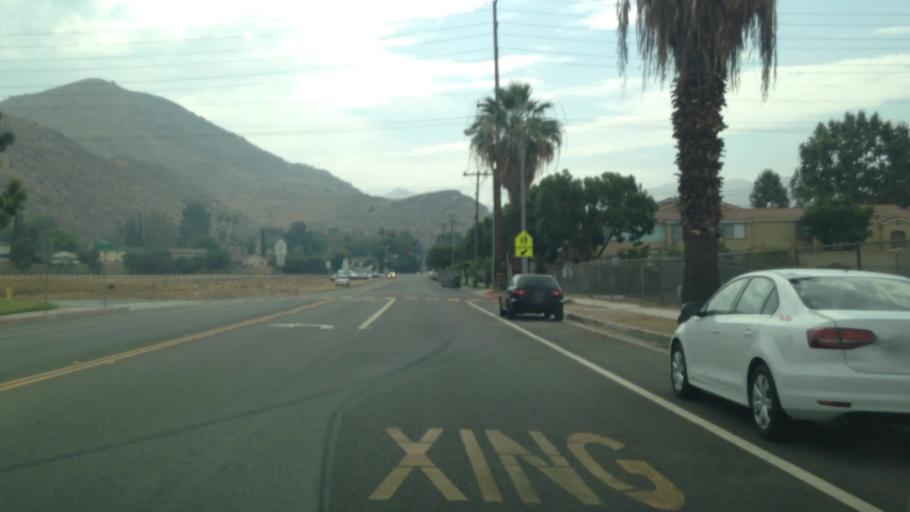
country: US
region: California
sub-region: Riverside County
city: Highgrove
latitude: 33.9902
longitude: -117.3362
